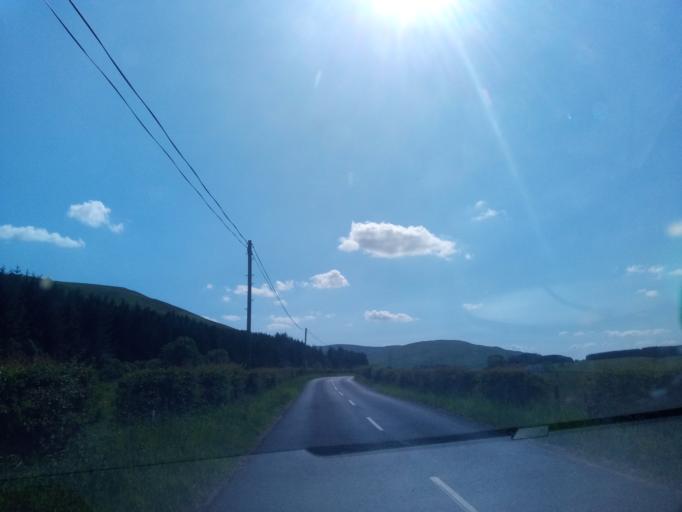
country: GB
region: Scotland
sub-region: The Scottish Borders
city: Innerleithen
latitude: 55.5149
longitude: -3.0892
